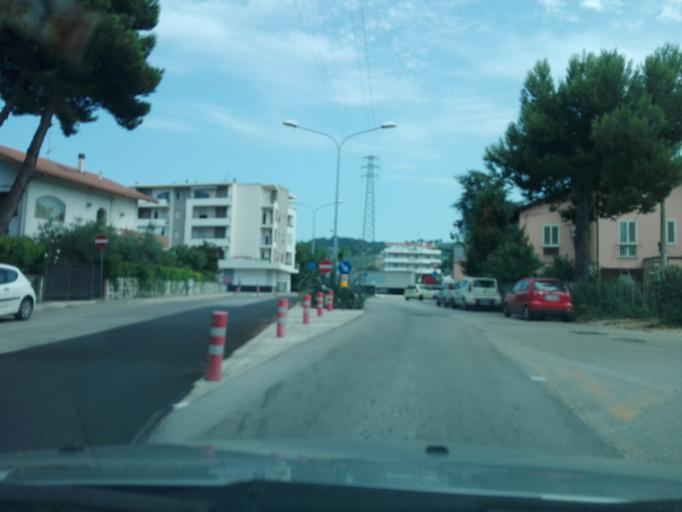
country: IT
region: Abruzzo
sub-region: Provincia di Pescara
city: Montesilvano Marina
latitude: 42.5033
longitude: 14.1346
